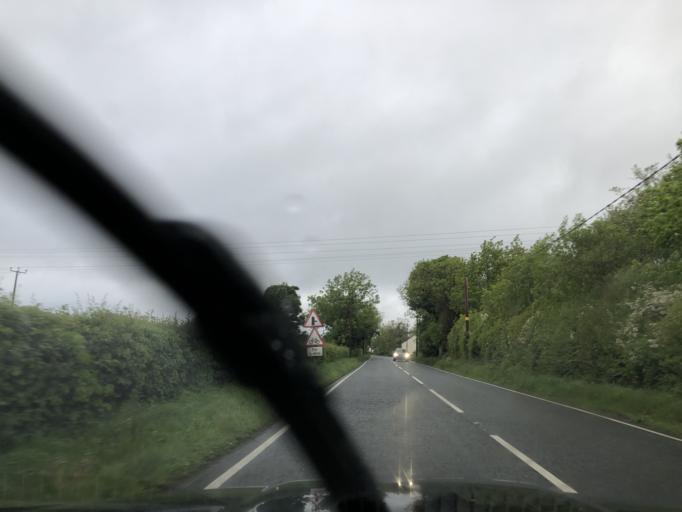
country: GB
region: Northern Ireland
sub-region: Antrim Borough
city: Antrim
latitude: 54.6765
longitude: -6.2219
